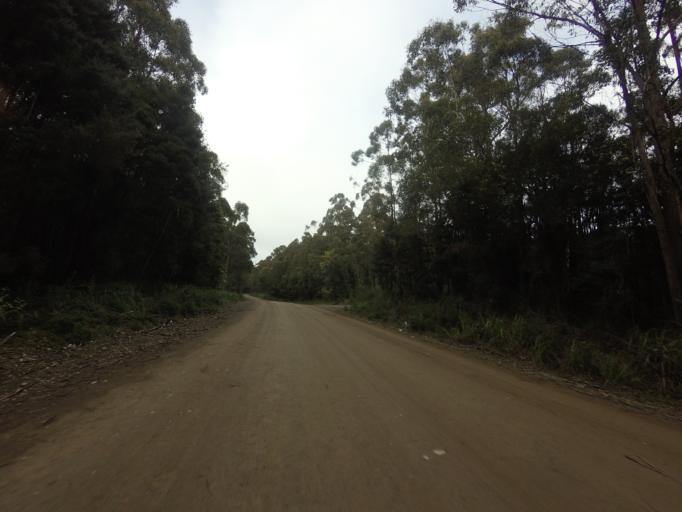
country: AU
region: Tasmania
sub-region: Huon Valley
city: Geeveston
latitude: -43.5131
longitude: 146.8854
